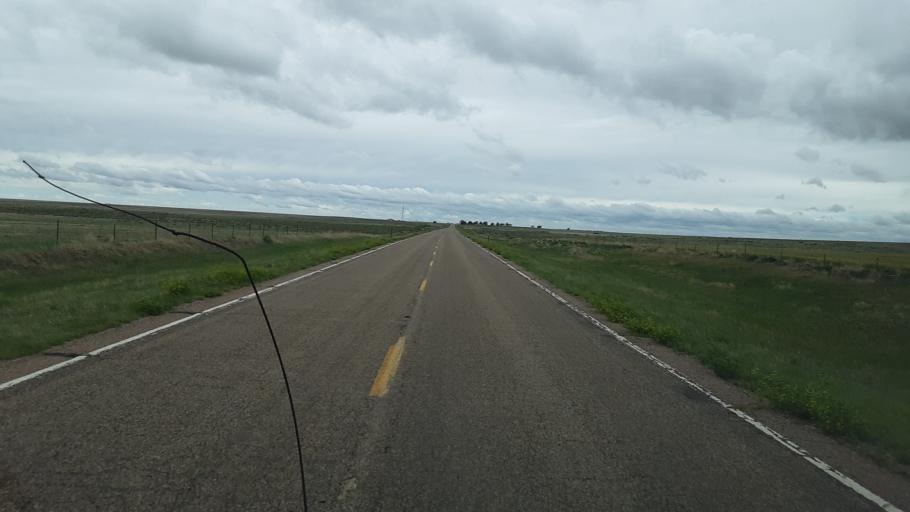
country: US
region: Colorado
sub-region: Lincoln County
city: Hugo
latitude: 38.8518
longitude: -103.6797
